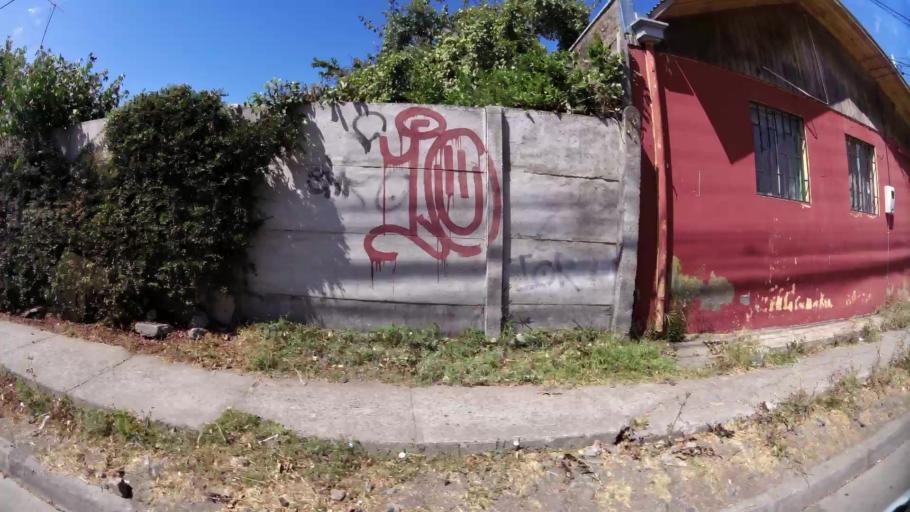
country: CL
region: Maule
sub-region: Provincia de Curico
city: Curico
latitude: -34.9672
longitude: -71.2440
